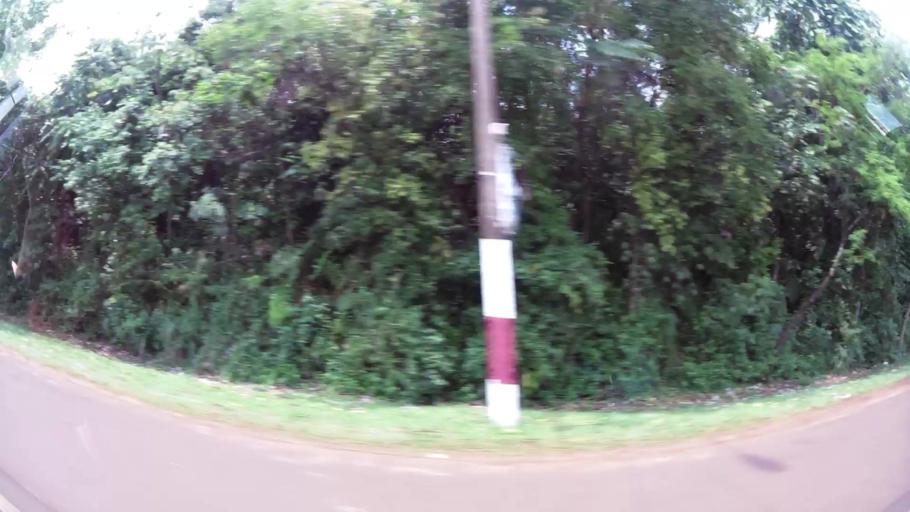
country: PY
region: Alto Parana
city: Ciudad del Este
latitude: -25.4801
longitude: -54.6260
